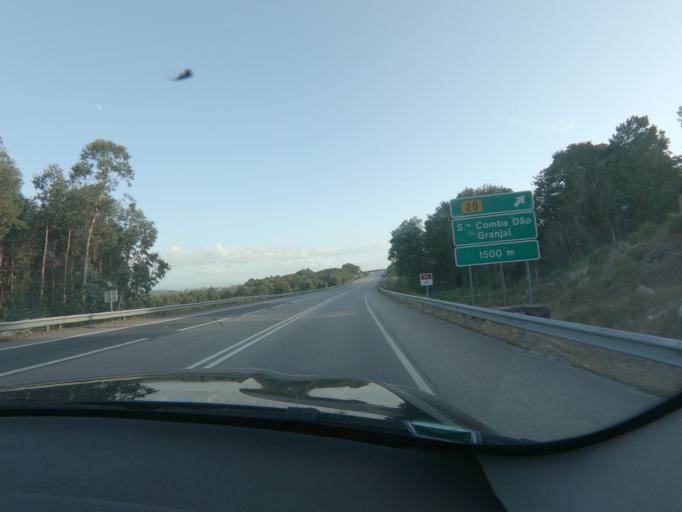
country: PT
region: Viseu
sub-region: Santa Comba Dao
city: Santa Comba Dao
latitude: 40.4134
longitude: -8.1225
